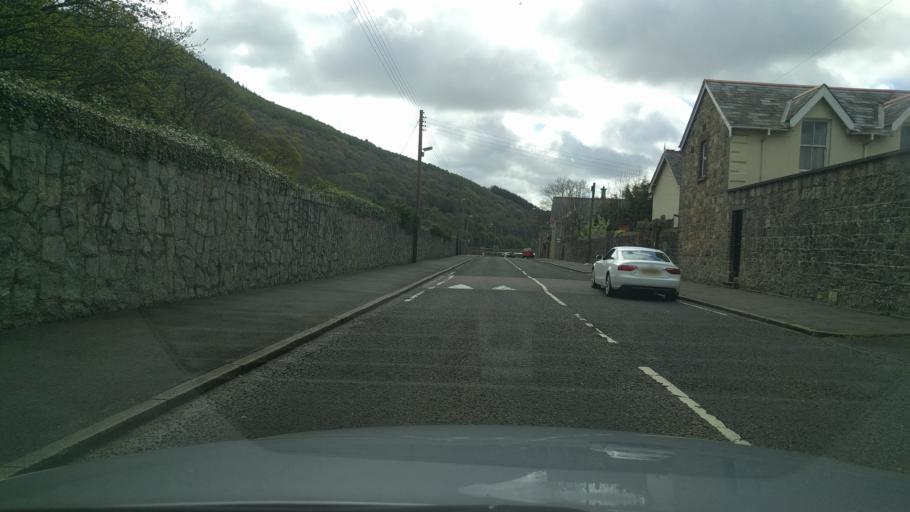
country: GB
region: Northern Ireland
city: Rostrevor
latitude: 54.0970
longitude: -6.1939
